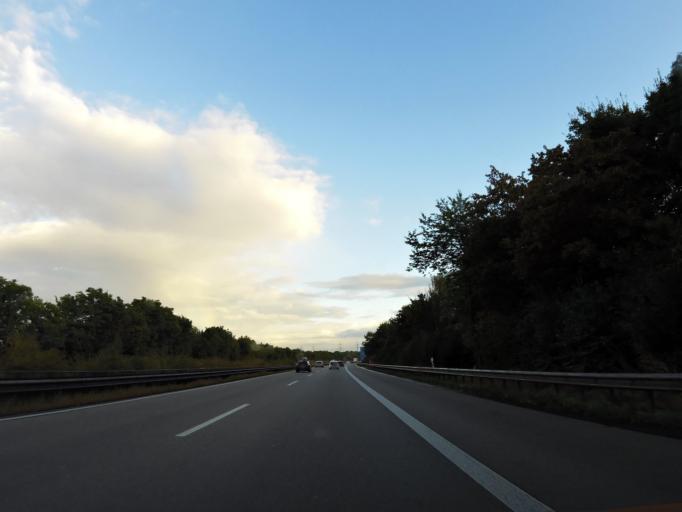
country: DE
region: Rheinland-Pfalz
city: Lonsheim
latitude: 49.7865
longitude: 8.0990
